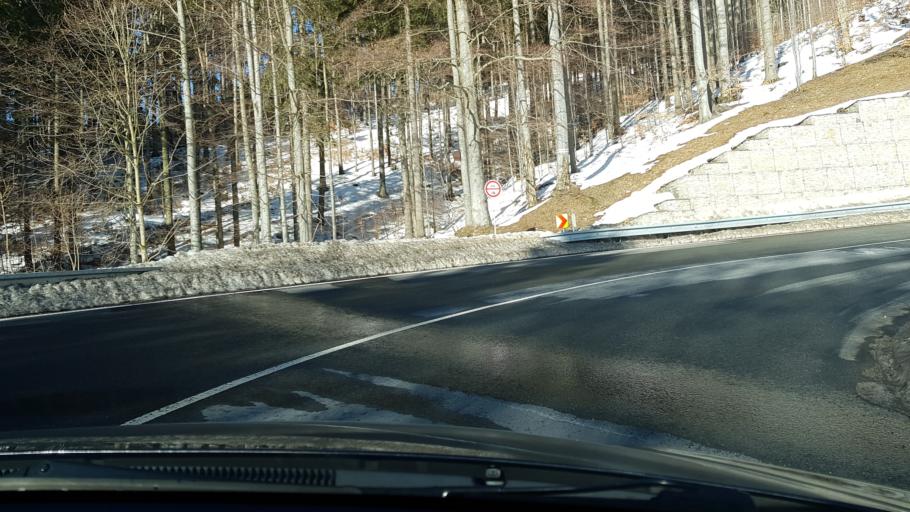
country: CZ
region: Olomoucky
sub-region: Okres Sumperk
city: Loucna nad Desnou
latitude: 50.1115
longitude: 17.1415
